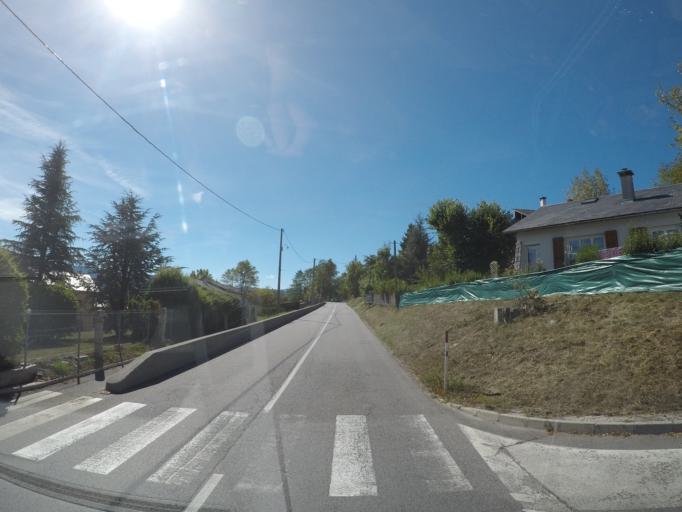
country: FR
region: Languedoc-Roussillon
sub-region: Departement des Pyrenees-Orientales
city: la Guingueta d'Ix
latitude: 42.4607
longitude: 1.9362
